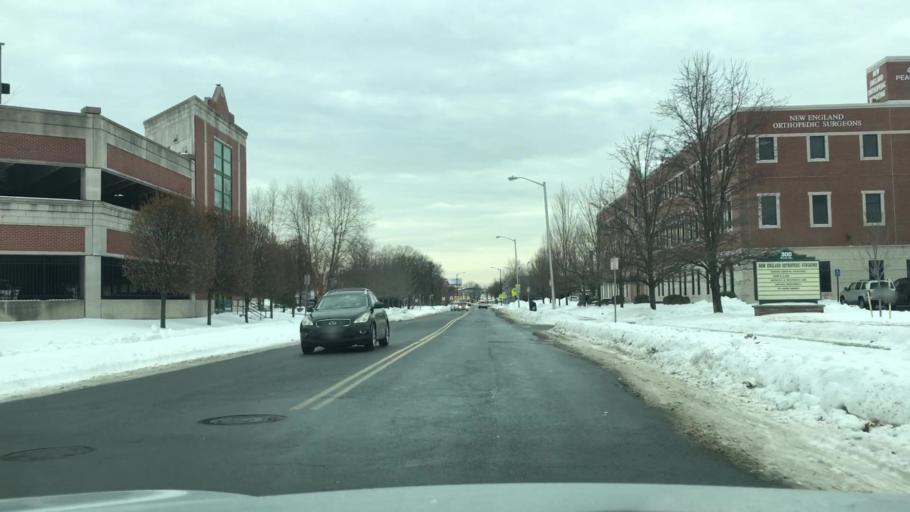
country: US
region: Massachusetts
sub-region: Hampden County
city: West Springfield
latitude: 42.1218
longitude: -72.6110
